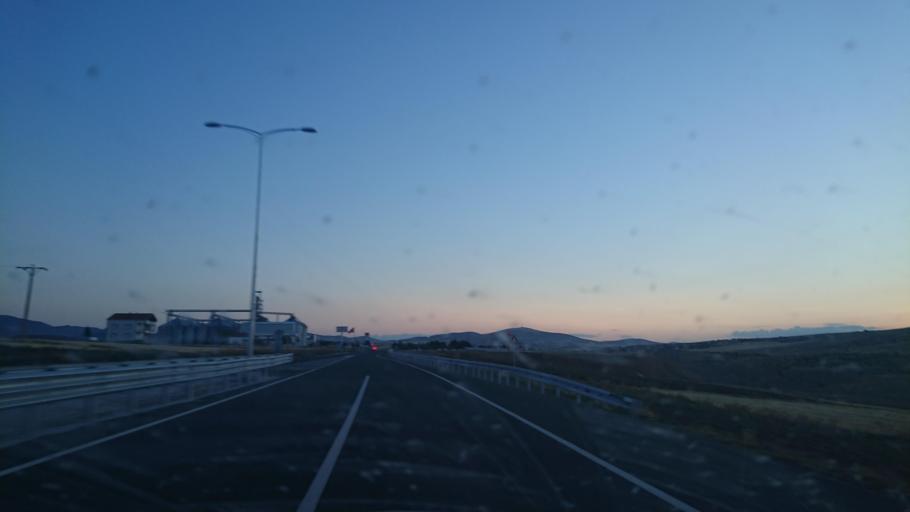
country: TR
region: Aksaray
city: Balci
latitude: 38.7676
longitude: 34.0963
